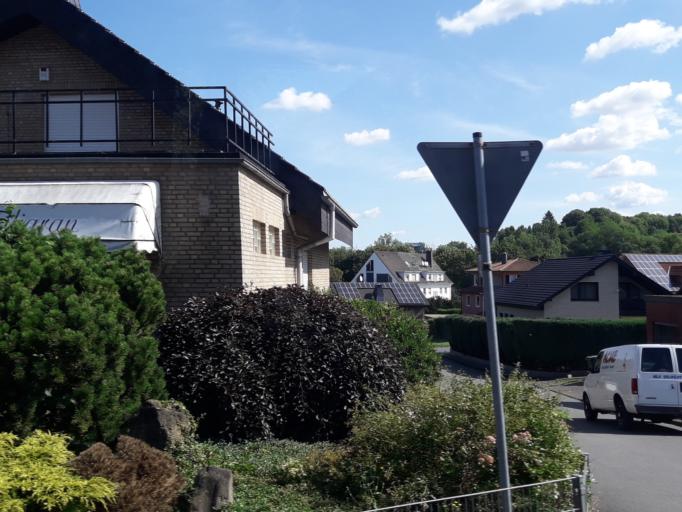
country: DE
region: North Rhine-Westphalia
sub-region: Regierungsbezirk Detmold
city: Paderborn
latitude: 51.6554
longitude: 8.7210
